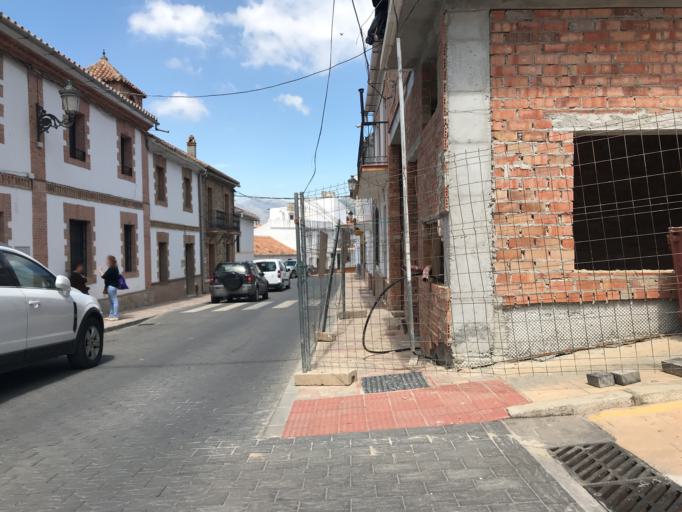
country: ES
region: Andalusia
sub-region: Provincia de Malaga
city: Periana
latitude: 36.9267
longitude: -4.1907
